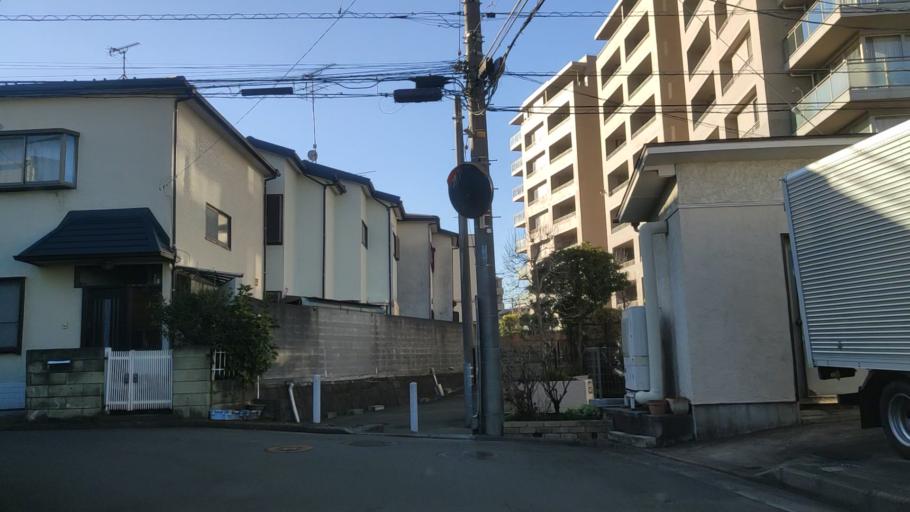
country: JP
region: Tokyo
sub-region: Machida-shi
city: Machida
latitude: 35.5176
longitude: 139.5473
